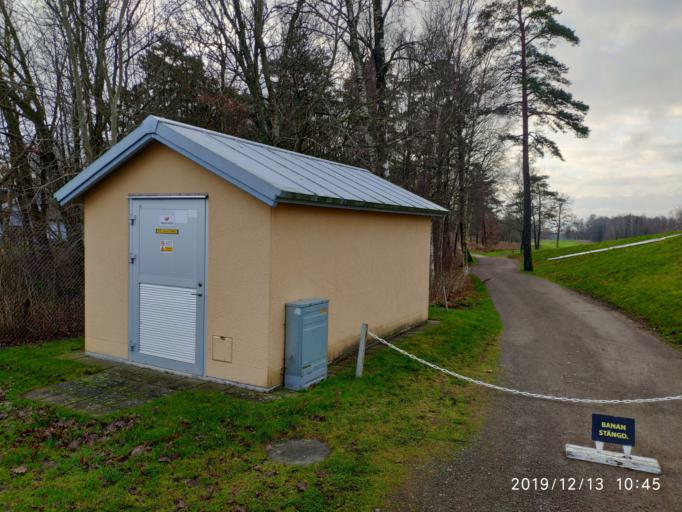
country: SE
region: Halland
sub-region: Varbergs Kommun
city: Tvaaker
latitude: 57.0638
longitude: 12.3507
